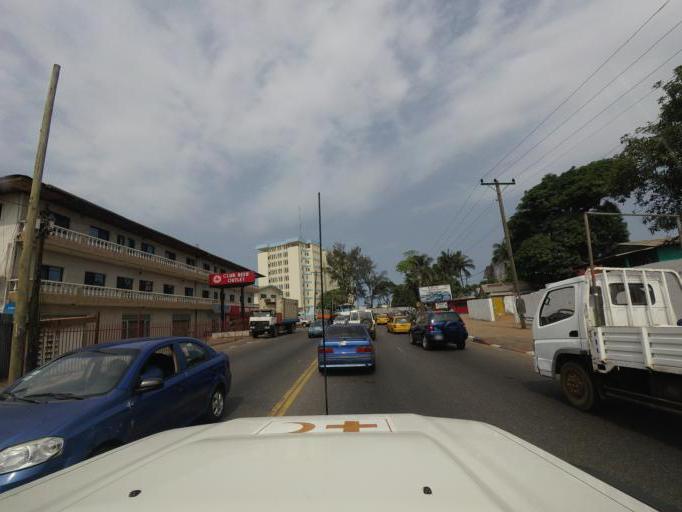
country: LR
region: Montserrado
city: Monrovia
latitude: 6.2947
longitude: -10.7927
